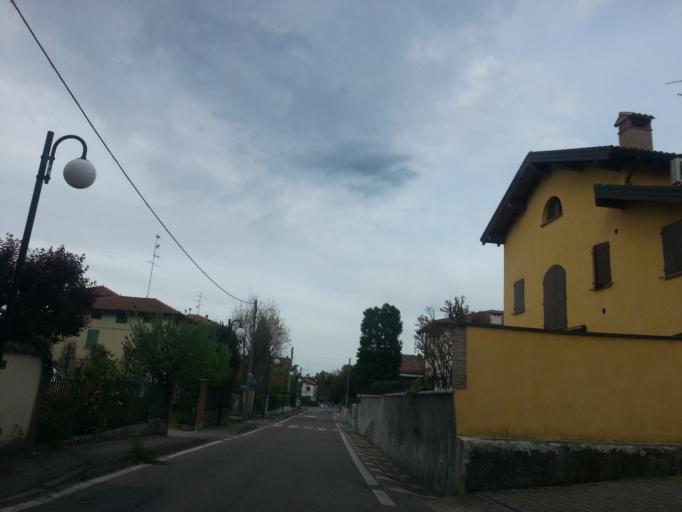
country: IT
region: Emilia-Romagna
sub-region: Provincia di Reggio Emilia
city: Albinea
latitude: 44.6232
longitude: 10.5912
